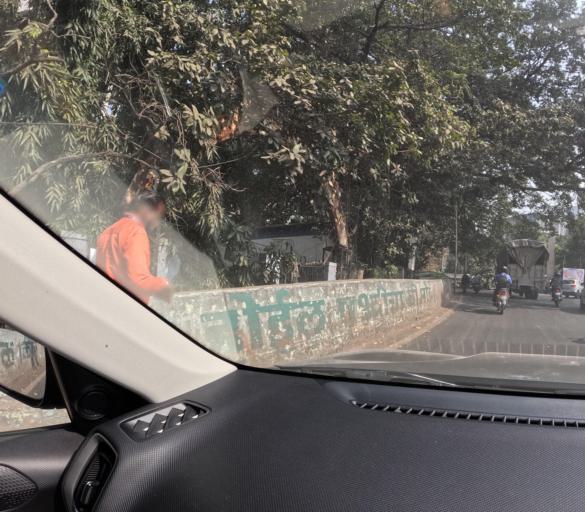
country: IN
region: Maharashtra
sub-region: Pune Division
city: Pune
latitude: 18.5245
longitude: 73.8697
